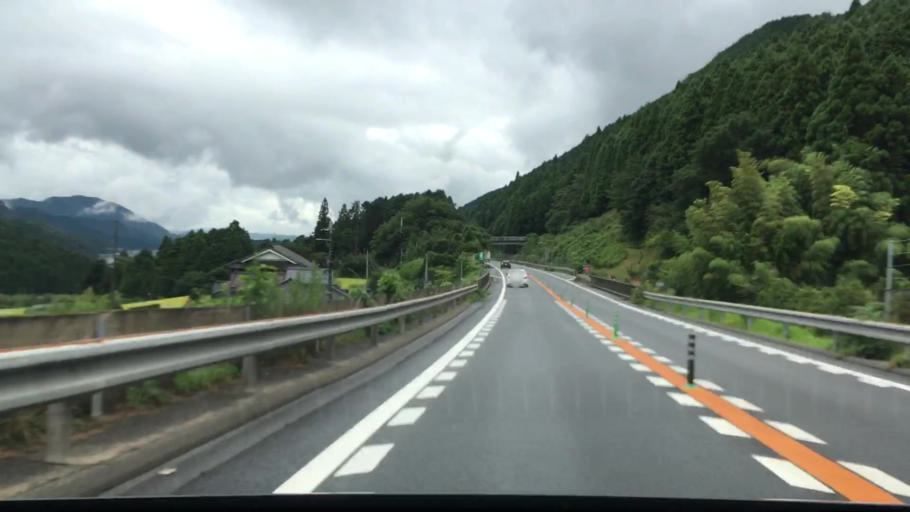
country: JP
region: Hyogo
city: Nishiwaki
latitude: 35.1092
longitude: 134.7804
